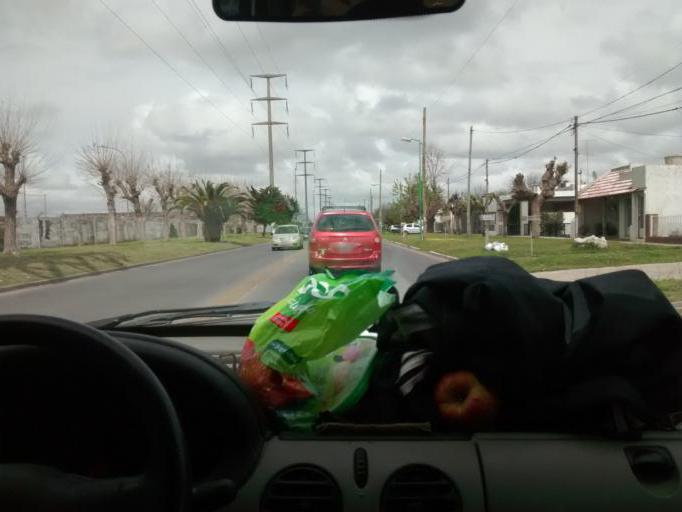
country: AR
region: Buenos Aires
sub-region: Partido de La Plata
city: La Plata
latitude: -34.9403
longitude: -57.9740
